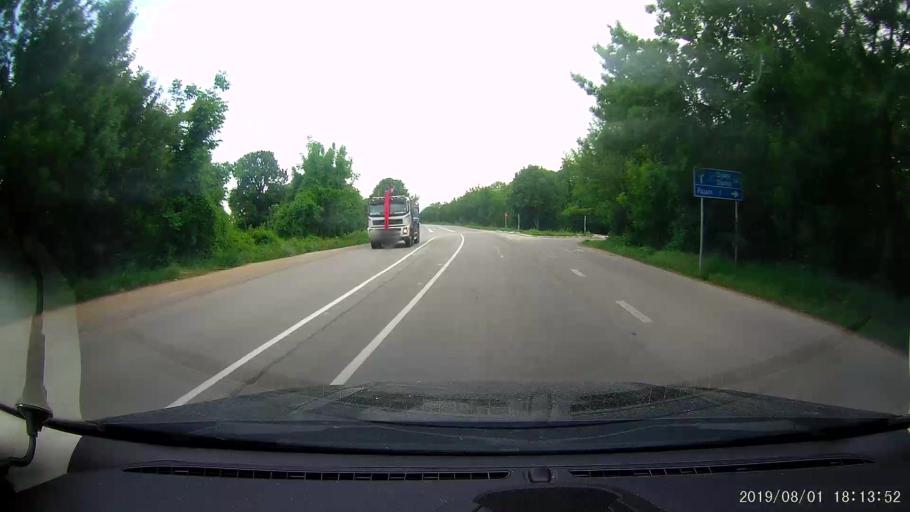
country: BG
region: Silistra
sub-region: Obshtina Dulovo
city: Dulovo
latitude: 43.7810
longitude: 27.1312
